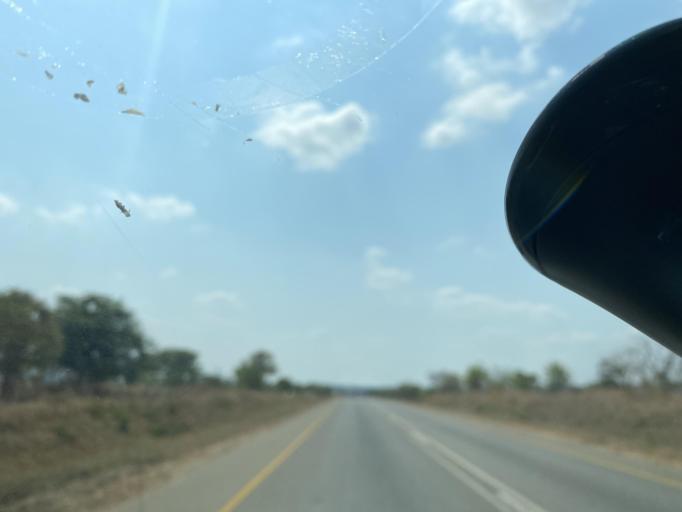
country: ZM
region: Lusaka
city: Chongwe
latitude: -15.5496
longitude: 28.6740
